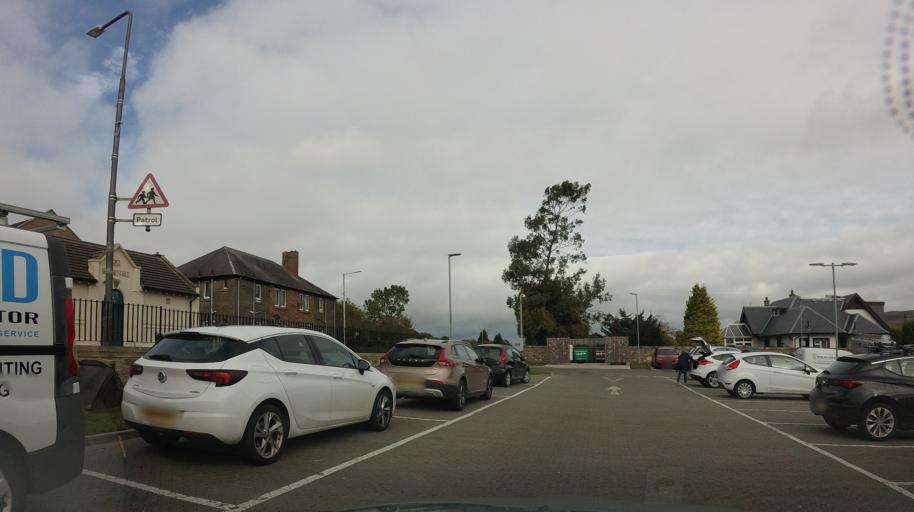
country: GB
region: Scotland
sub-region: Fife
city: Kelty
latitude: 56.1364
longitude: -3.3817
